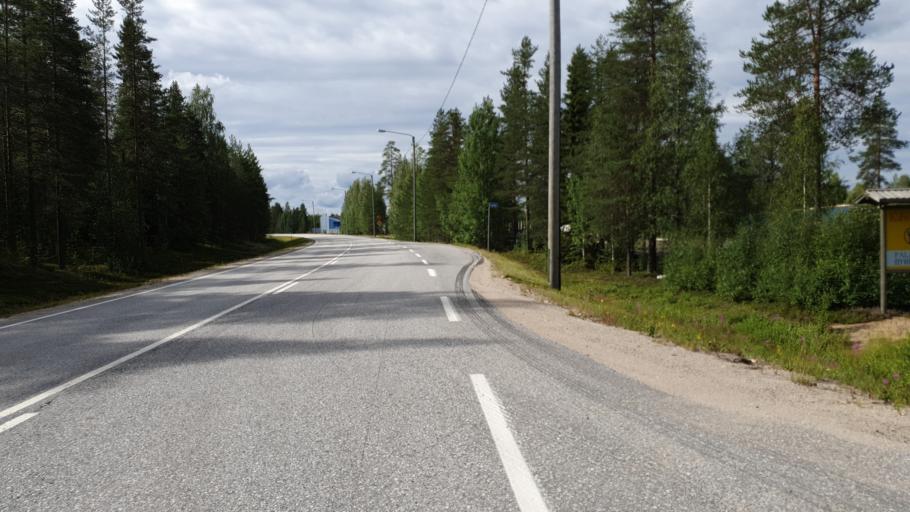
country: FI
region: Kainuu
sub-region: Kehys-Kainuu
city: Kuhmo
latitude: 64.5373
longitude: 29.9455
